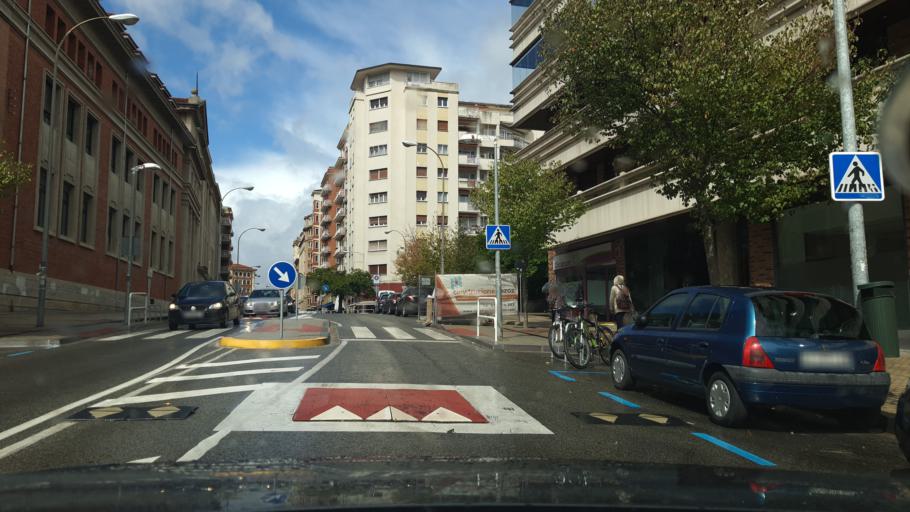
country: ES
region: Navarre
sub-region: Provincia de Navarra
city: Segundo Ensanche
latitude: 42.8078
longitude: -1.6361
